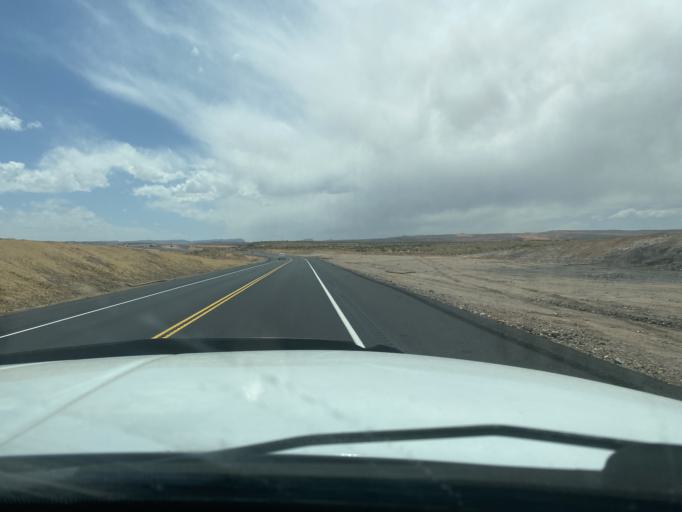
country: US
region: Utah
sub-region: Washington County
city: Hurricane
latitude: 37.1376
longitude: -113.3476
